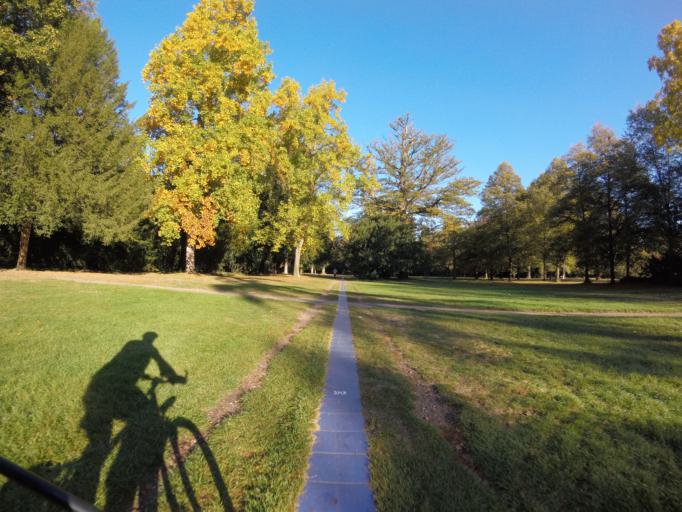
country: DE
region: Baden-Wuerttemberg
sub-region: Karlsruhe Region
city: Karlsruhe
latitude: 49.0159
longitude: 8.4035
